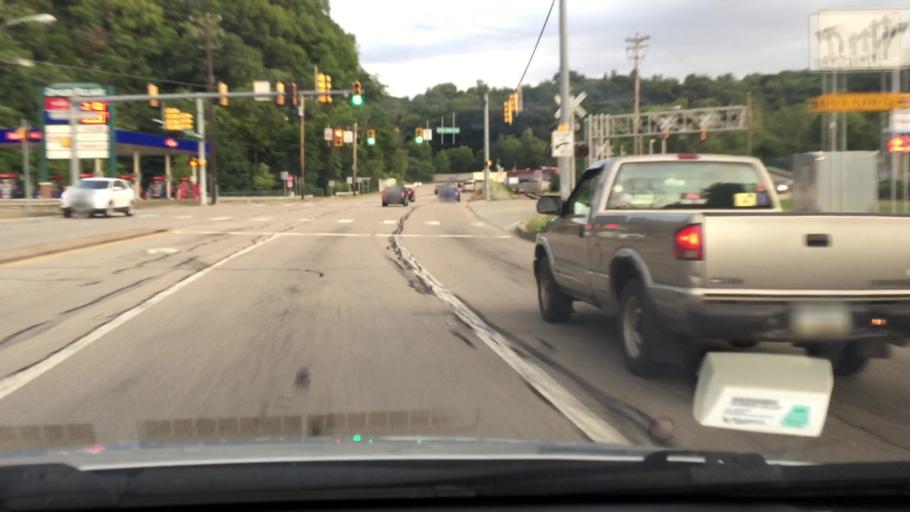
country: US
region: Pennsylvania
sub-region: Allegheny County
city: Glenshaw
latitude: 40.5390
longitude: -79.9626
